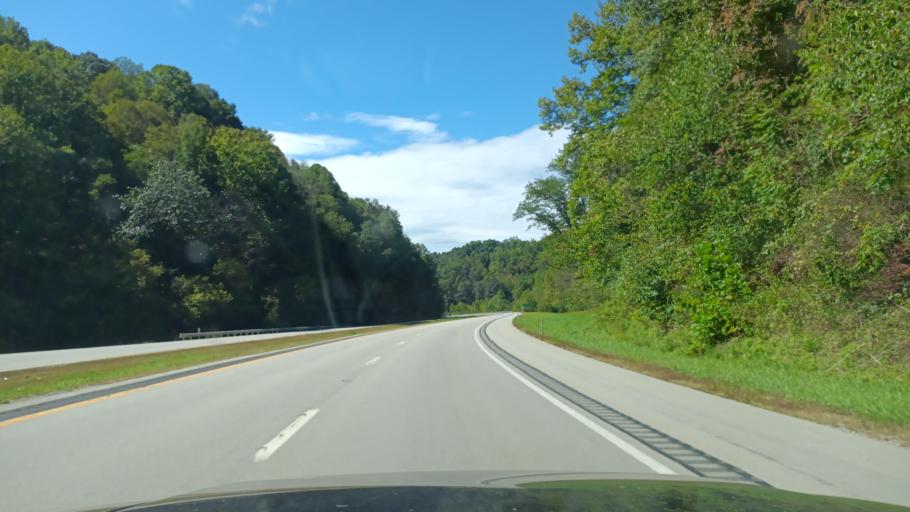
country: US
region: West Virginia
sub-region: Harrison County
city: Salem
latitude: 39.2833
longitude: -80.6635
